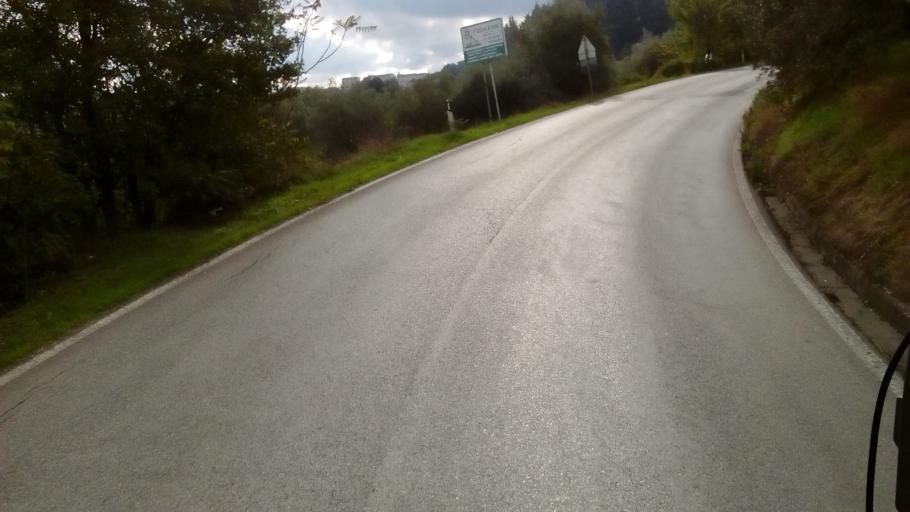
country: IT
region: Tuscany
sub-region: Province of Florence
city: Montespertoli
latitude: 43.6487
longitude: 11.0857
